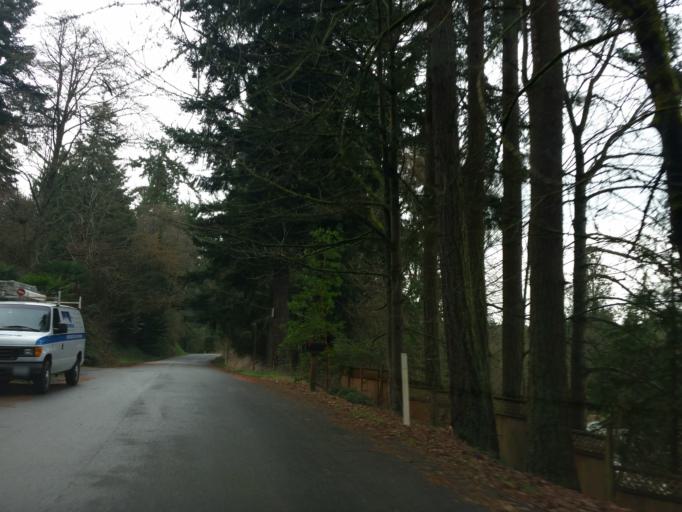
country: US
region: Washington
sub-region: King County
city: Shoreline
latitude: 47.7540
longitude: -122.3577
